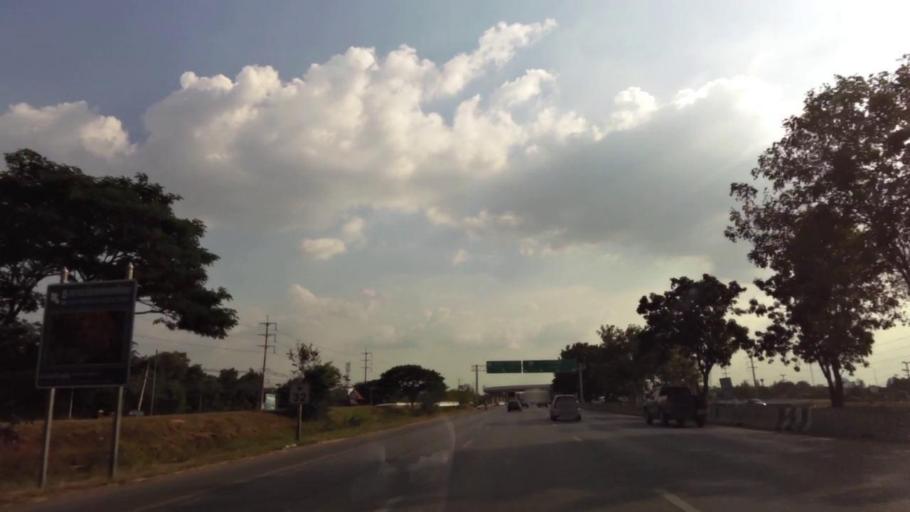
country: TH
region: Phra Nakhon Si Ayutthaya
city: Phra Nakhon Si Ayutthaya
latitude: 14.3604
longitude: 100.6129
